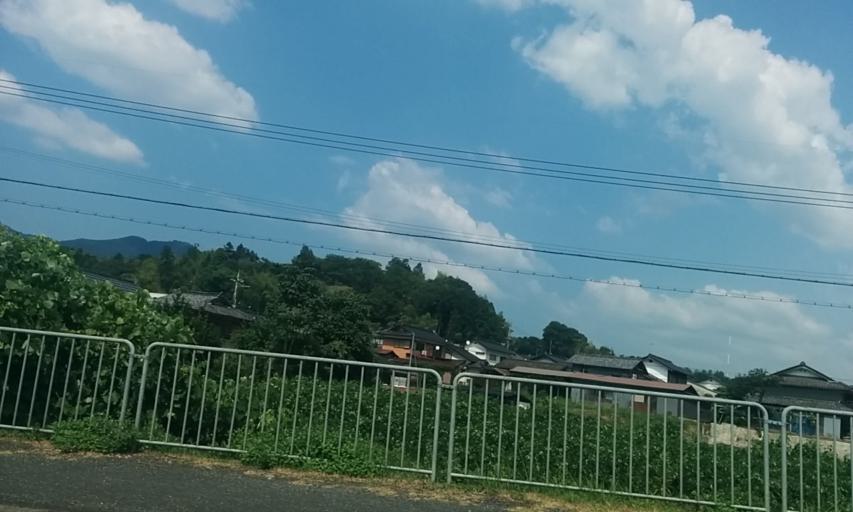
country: JP
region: Kyoto
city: Fukuchiyama
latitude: 35.3057
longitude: 135.1304
